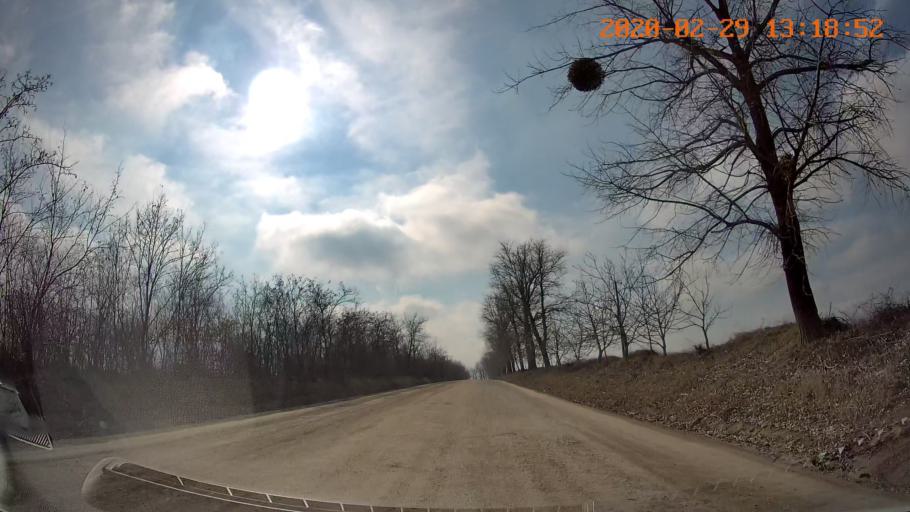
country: MD
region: Telenesti
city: Camenca
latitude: 47.9920
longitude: 28.6549
